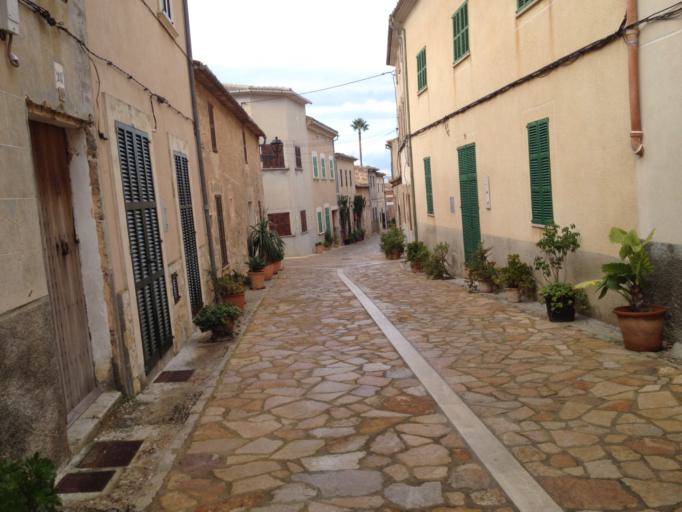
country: ES
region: Balearic Islands
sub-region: Illes Balears
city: Petra
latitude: 39.6104
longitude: 3.1114
